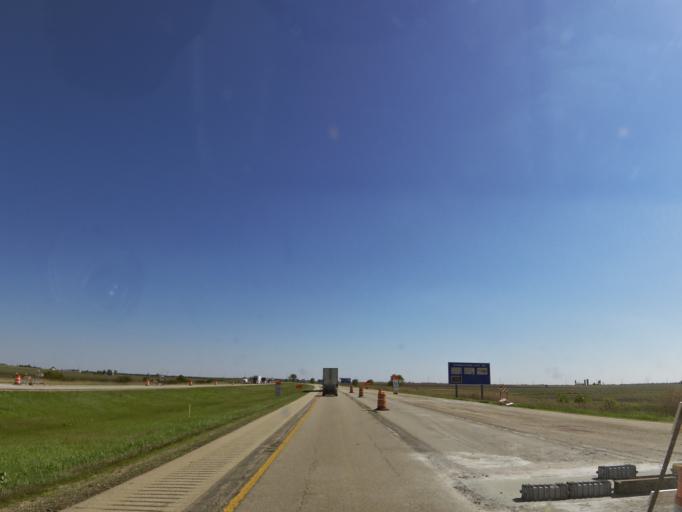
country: US
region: Illinois
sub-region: Ogle County
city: Hillcrest
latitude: 41.9631
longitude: -89.0239
